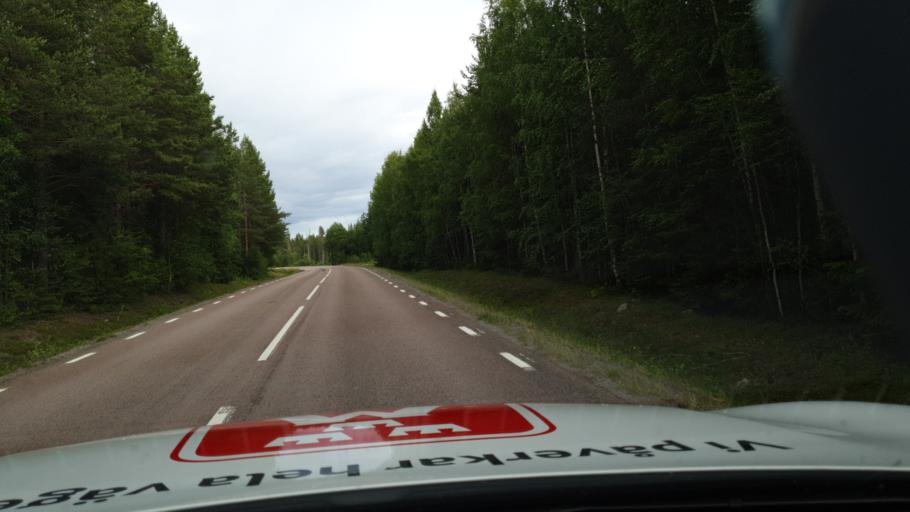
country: SE
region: Jaemtland
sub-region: Stroemsunds Kommun
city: Stroemsund
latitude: 63.6348
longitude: 16.0420
